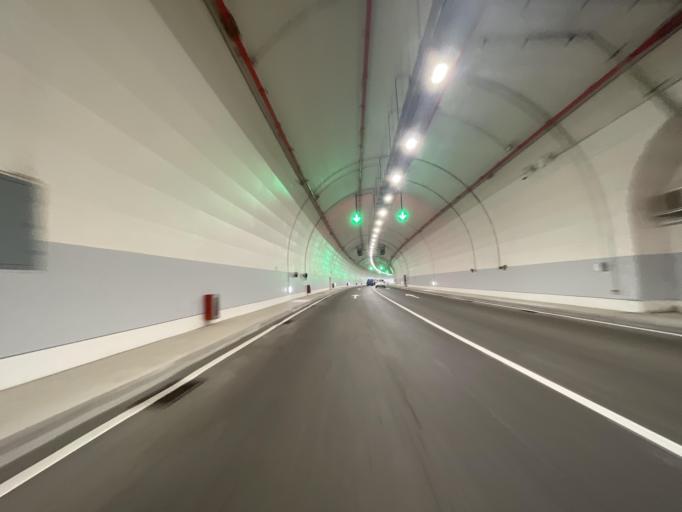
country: MO
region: Macau
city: Macau
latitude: 22.1361
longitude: 113.5782
